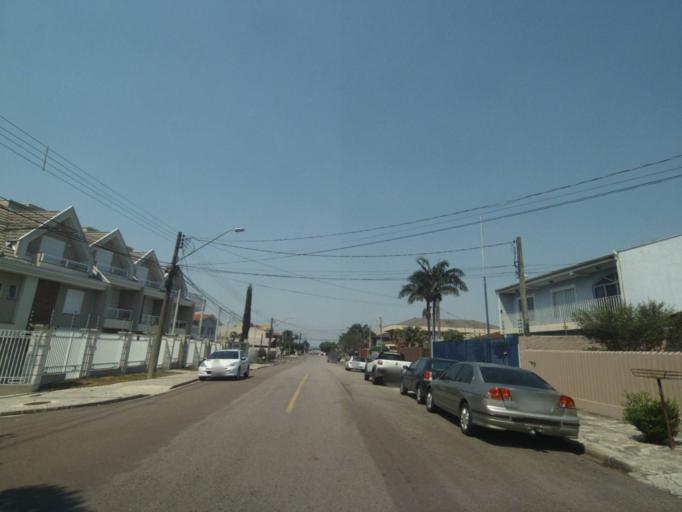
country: BR
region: Parana
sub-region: Sao Jose Dos Pinhais
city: Sao Jose dos Pinhais
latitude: -25.5063
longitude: -49.2729
